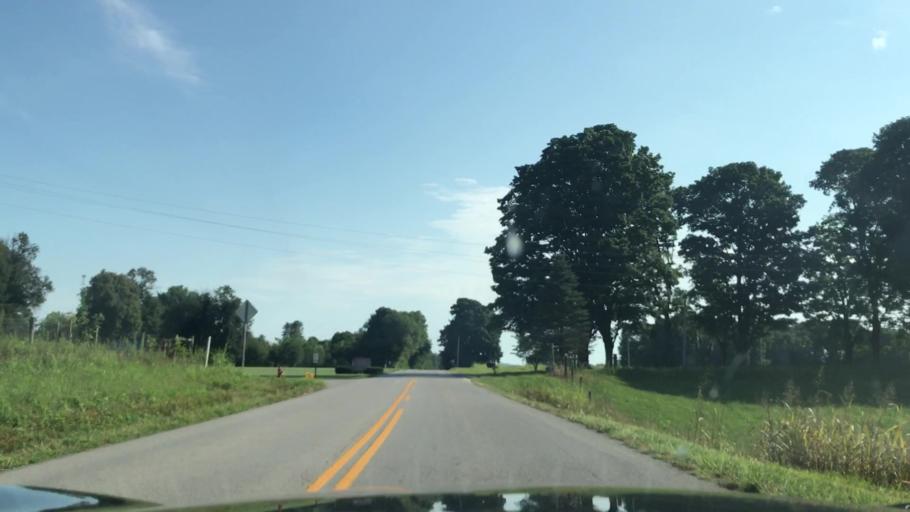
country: US
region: Kentucky
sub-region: Hart County
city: Horse Cave
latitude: 37.1698
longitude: -85.7950
